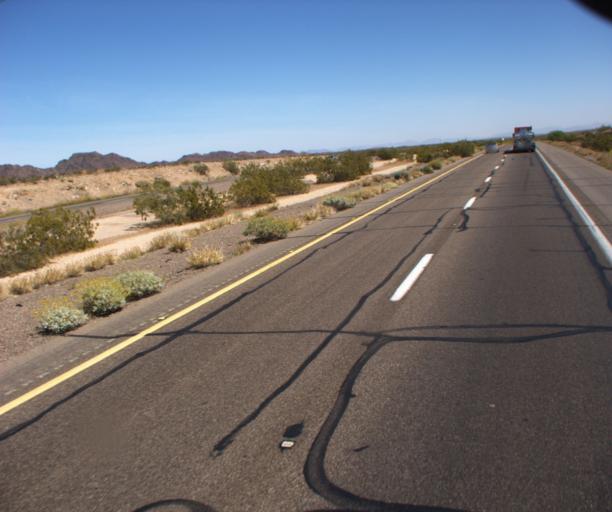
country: US
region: Arizona
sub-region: Maricopa County
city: Gila Bend
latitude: 32.8905
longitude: -113.0608
